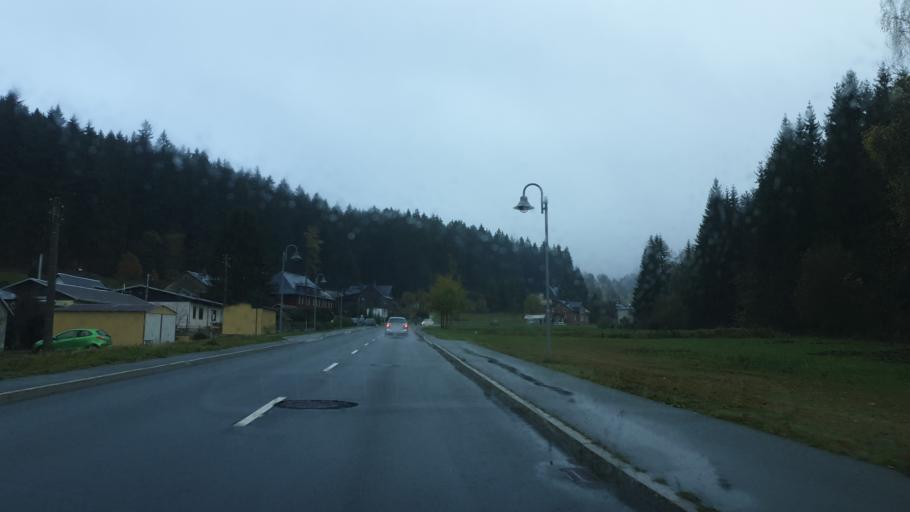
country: DE
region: Saxony
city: Tannenbergsthal
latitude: 50.4315
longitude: 12.4681
